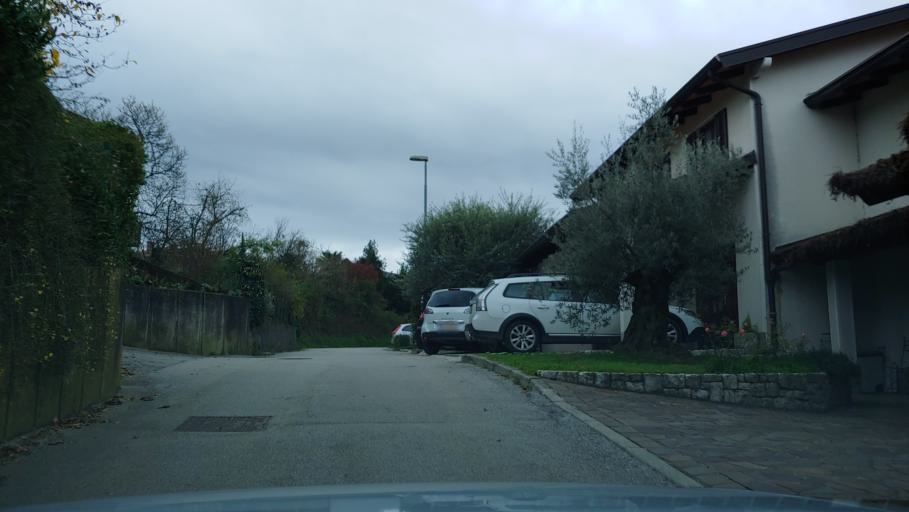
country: SI
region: Sempeter-Vrtojba
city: Sempeter pri Gorici
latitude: 45.9195
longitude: 13.6442
